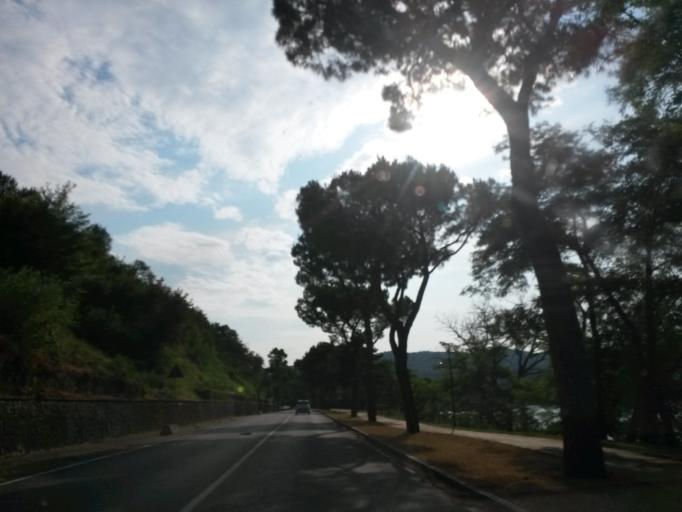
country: IT
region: Lombardy
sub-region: Provincia di Brescia
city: Padenghe sul Garda
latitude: 45.4891
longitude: 10.5280
